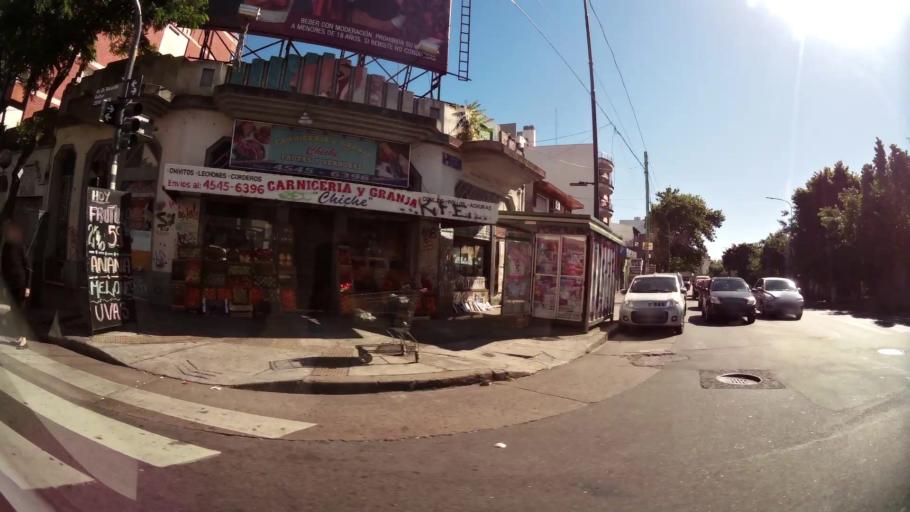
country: AR
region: Buenos Aires F.D.
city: Colegiales
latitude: -34.5600
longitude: -58.4715
